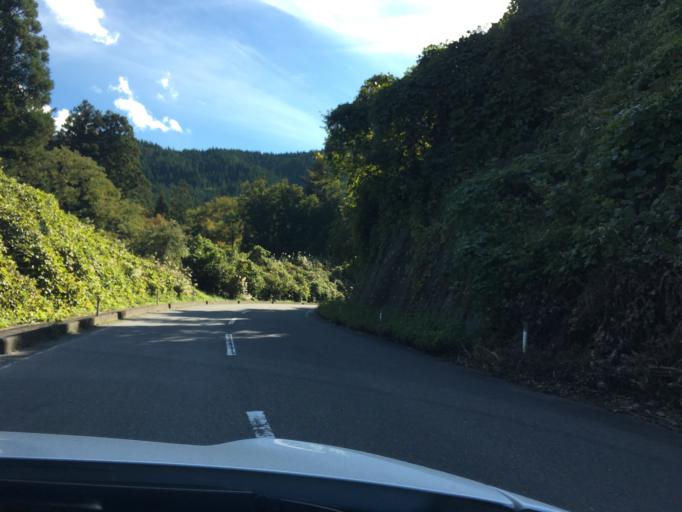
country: JP
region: Fukushima
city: Ishikawa
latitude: 37.1255
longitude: 140.5864
